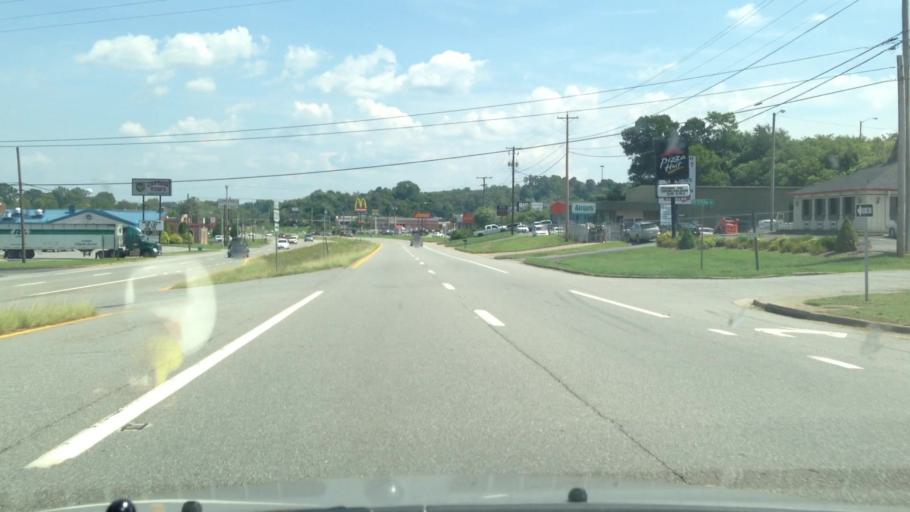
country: US
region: Virginia
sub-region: City of Martinsville
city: Martinsville
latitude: 36.6558
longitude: -79.8776
